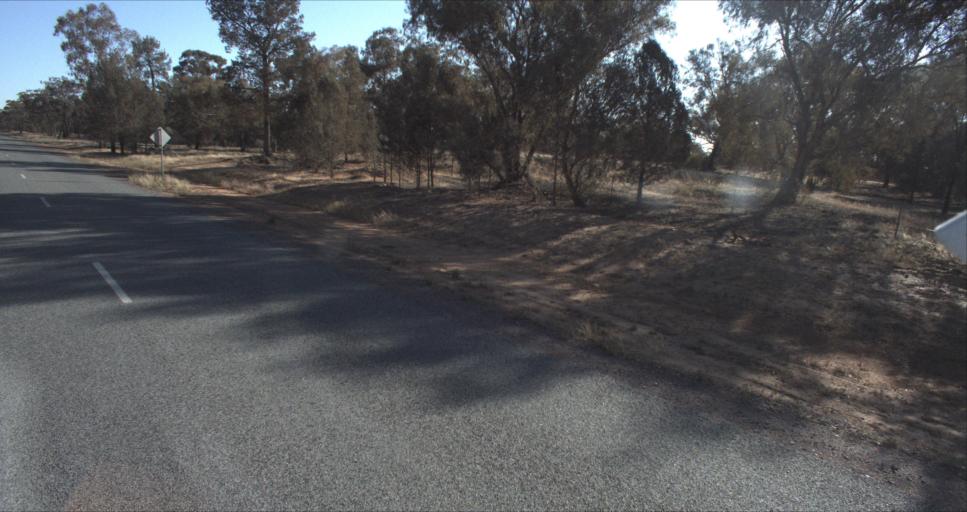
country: AU
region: New South Wales
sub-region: Leeton
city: Leeton
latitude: -34.6446
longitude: 146.3524
